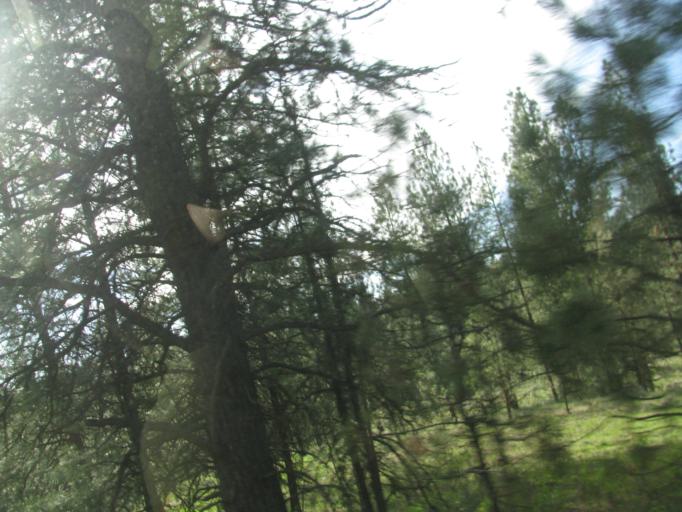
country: US
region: Washington
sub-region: Spokane County
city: Medical Lake
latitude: 47.3608
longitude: -117.8150
